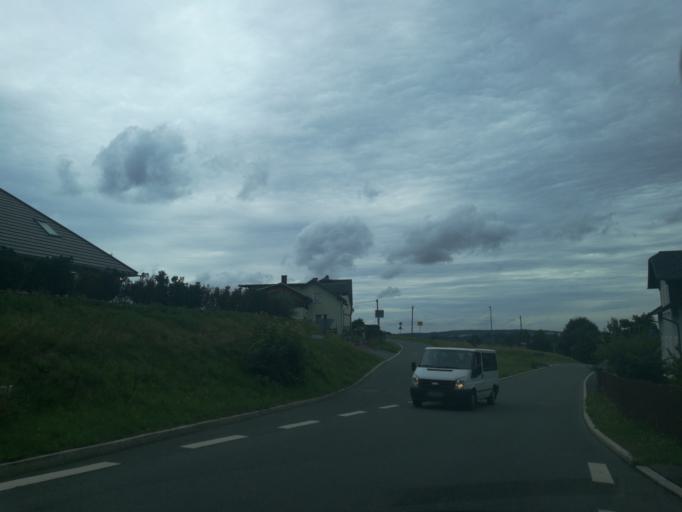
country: DE
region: Saxony
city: Adorf
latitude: 50.3111
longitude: 12.2692
